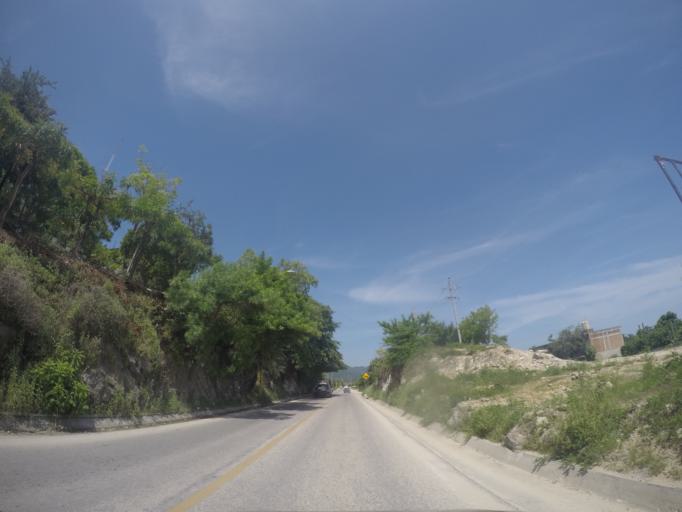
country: MX
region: Oaxaca
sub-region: Villa de Tututepec de Melchor Ocampo
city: Santa Rosa de Lima
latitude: 16.0107
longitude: -97.4434
